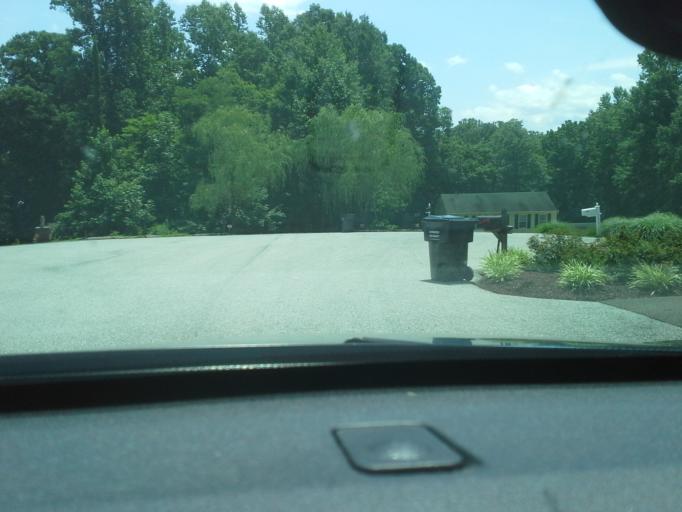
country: US
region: Maryland
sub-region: Calvert County
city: Dunkirk Town Center
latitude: 38.7107
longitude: -76.6552
